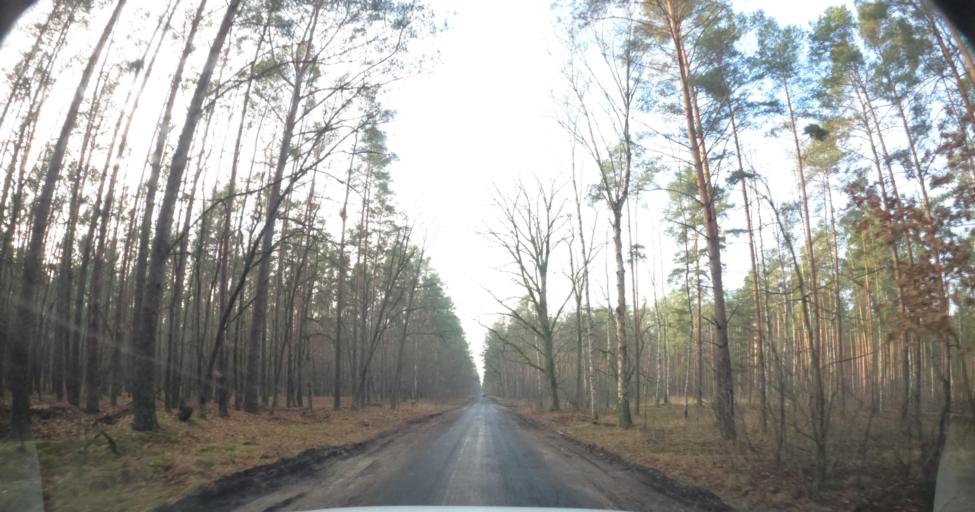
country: PL
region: West Pomeranian Voivodeship
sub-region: Powiat mysliborski
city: Boleszkowice
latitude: 52.7026
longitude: 14.5299
